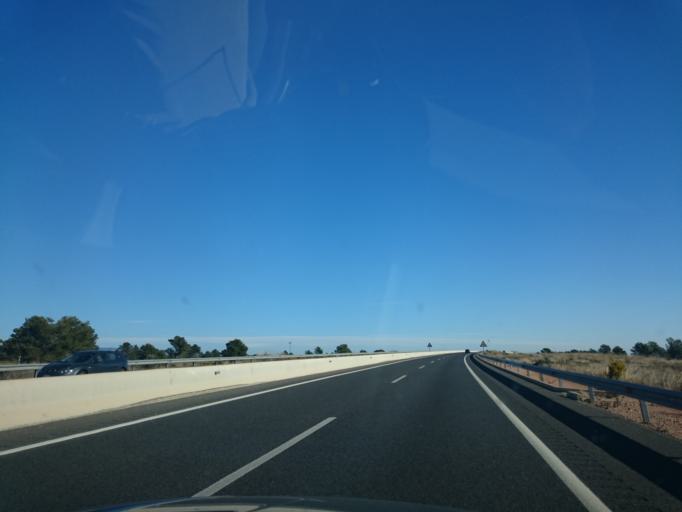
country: ES
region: Catalonia
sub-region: Provincia de Tarragona
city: Vilanova d'Escornalbou
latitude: 41.0366
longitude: 0.9470
